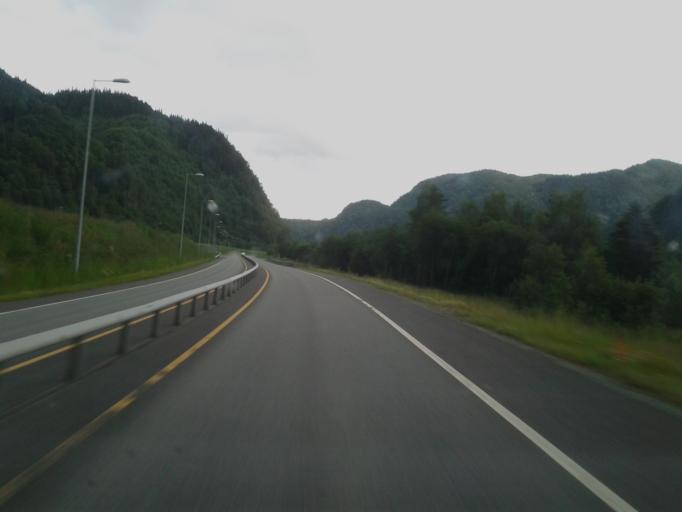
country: NO
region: Sor-Trondelag
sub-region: Midtre Gauldal
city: Storen
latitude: 63.0843
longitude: 10.2517
